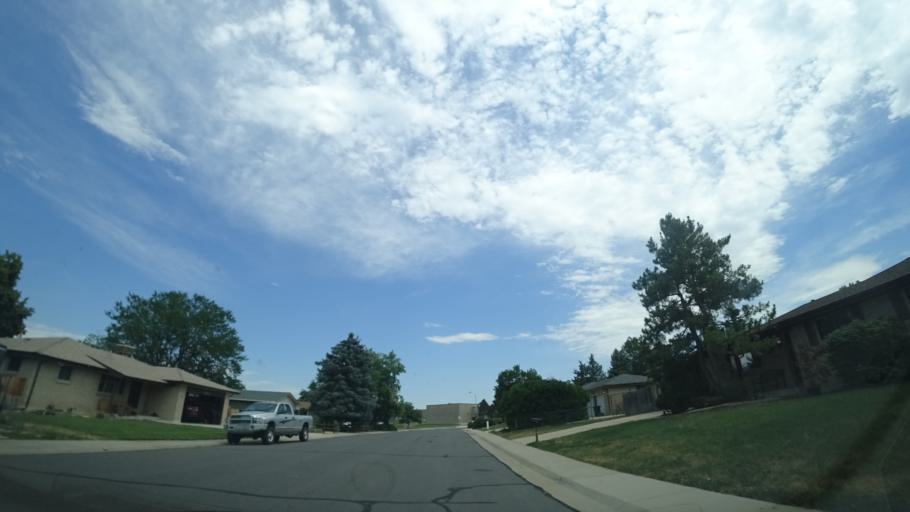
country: US
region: Colorado
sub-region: Jefferson County
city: Lakewood
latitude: 39.6923
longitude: -105.1065
